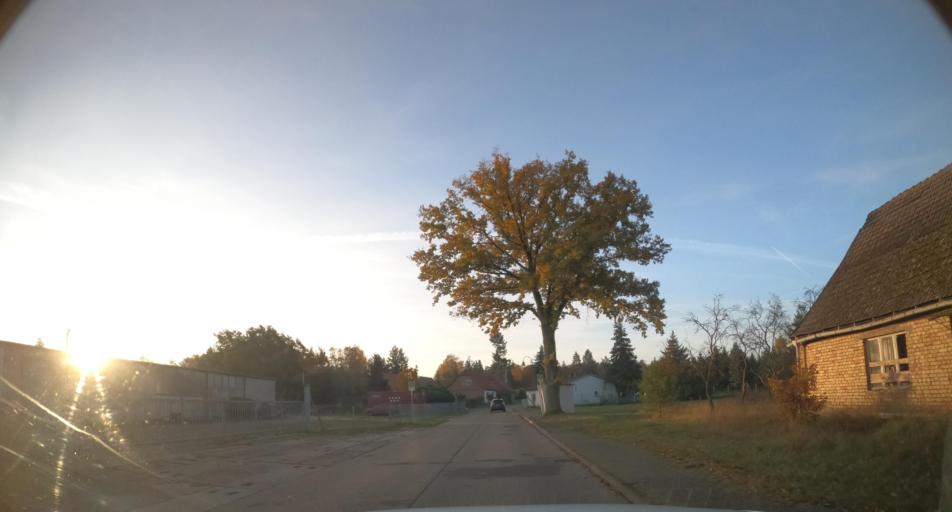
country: DE
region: Mecklenburg-Vorpommern
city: Ahlbeck
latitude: 53.6217
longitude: 14.2624
